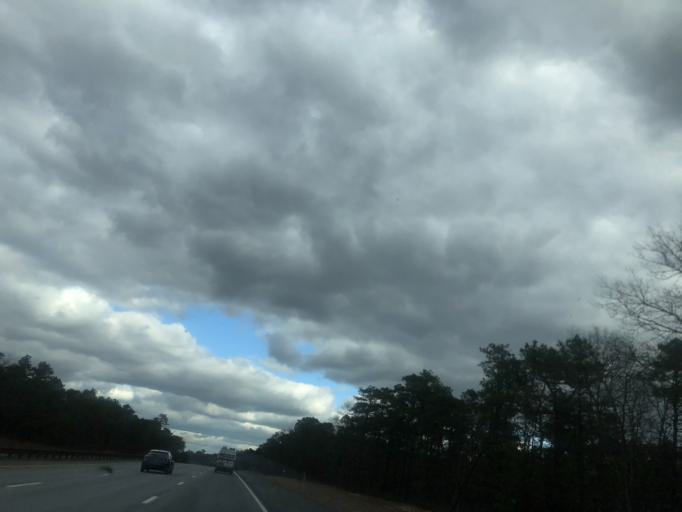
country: US
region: New Jersey
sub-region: Ocean County
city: Manahawkin
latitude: 39.6761
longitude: -74.3091
